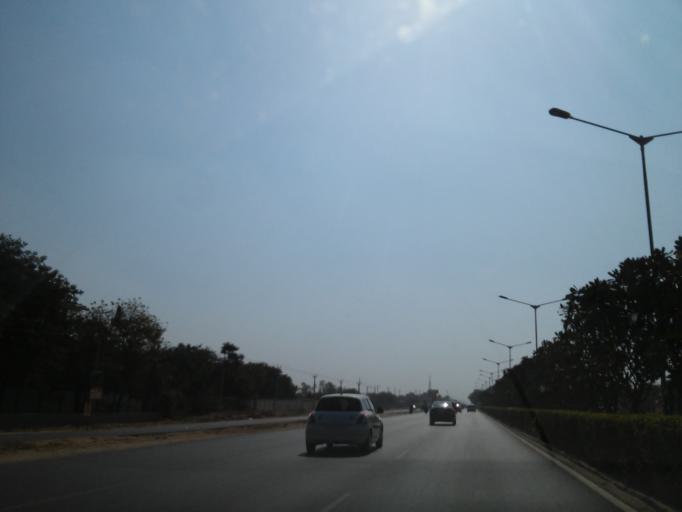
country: IN
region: Gujarat
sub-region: Gandhinagar
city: Adalaj
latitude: 23.1290
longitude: 72.5405
